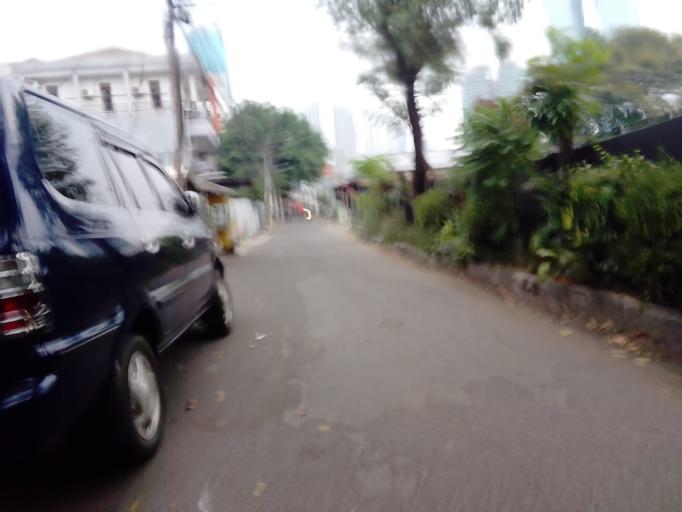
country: ID
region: Jakarta Raya
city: Jakarta
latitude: -6.1973
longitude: 106.8194
